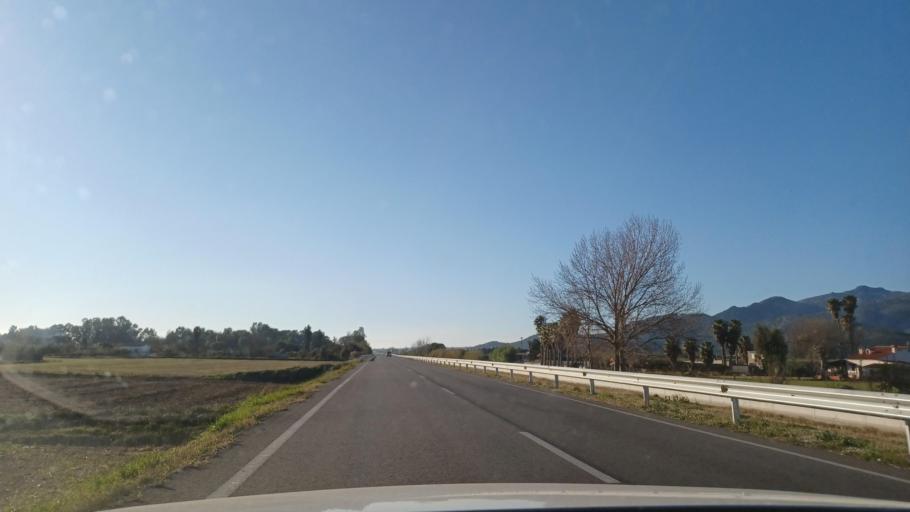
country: ES
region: Catalonia
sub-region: Provincia de Tarragona
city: Amposta
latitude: 40.6788
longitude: 0.5906
